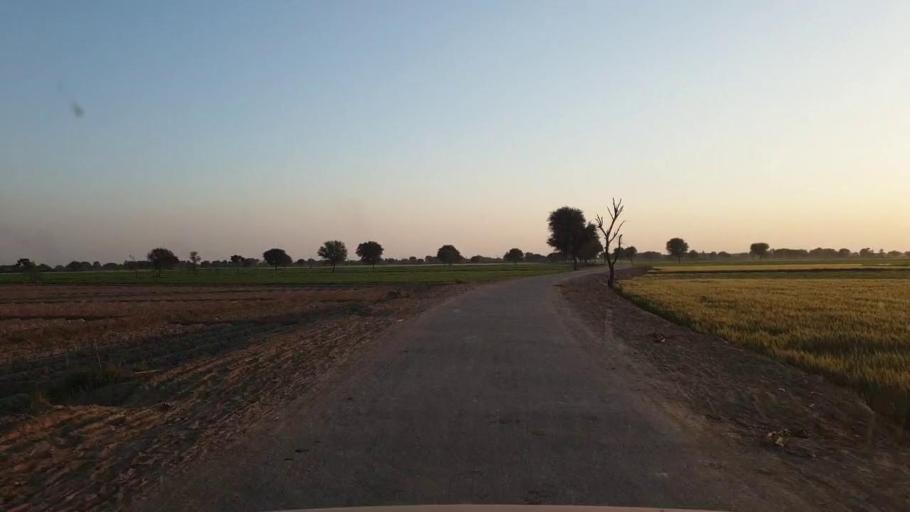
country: PK
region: Sindh
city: Tando Jam
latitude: 25.3105
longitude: 68.6402
